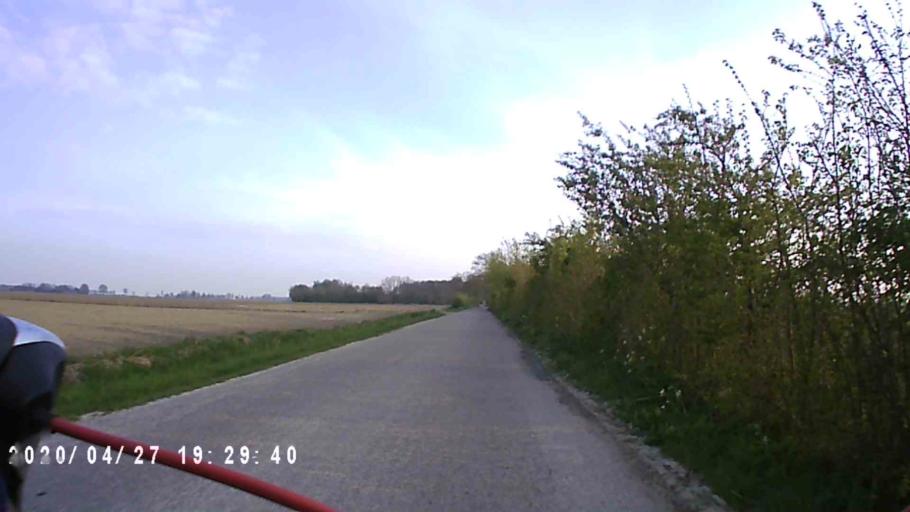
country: NL
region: Groningen
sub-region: Gemeente Winsum
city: Winsum
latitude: 53.3923
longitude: 6.4588
